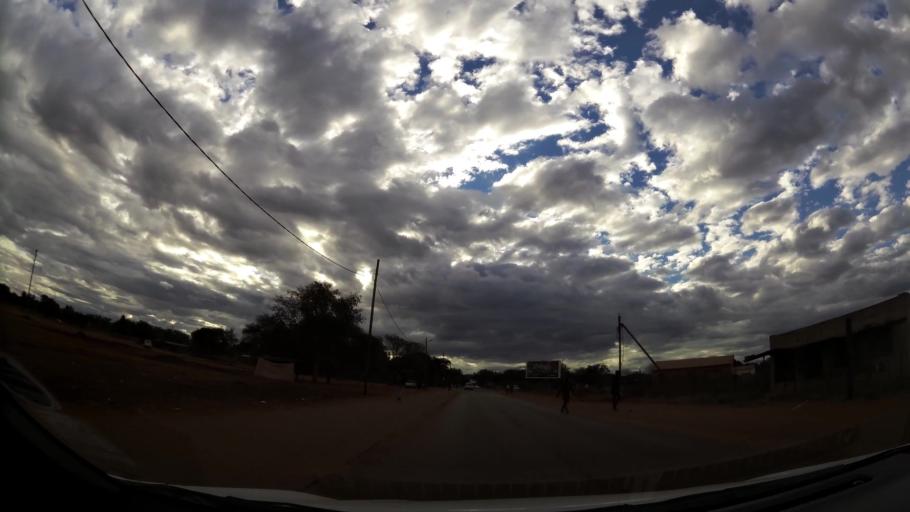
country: ZA
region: Limpopo
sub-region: Waterberg District Municipality
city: Modimolle
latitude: -24.5194
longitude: 28.7209
